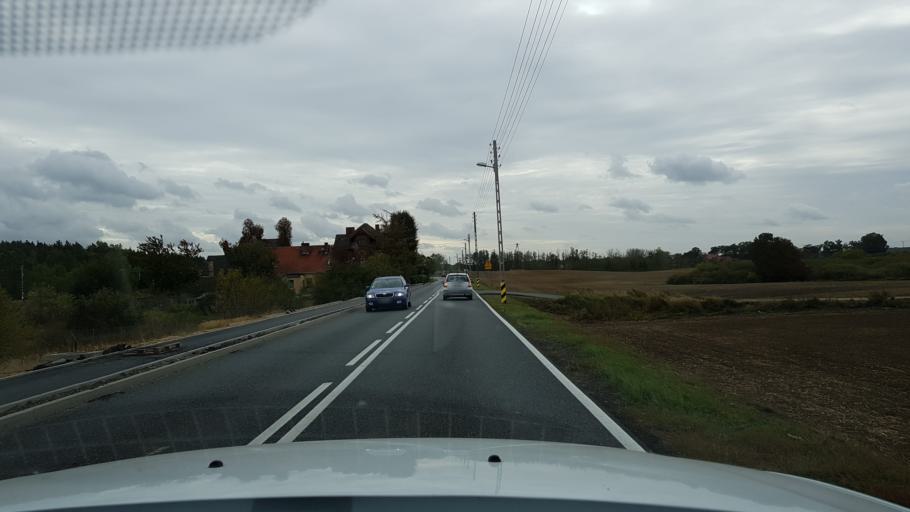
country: PL
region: West Pomeranian Voivodeship
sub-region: Powiat gryfinski
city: Chojna
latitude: 52.9045
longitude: 14.4563
